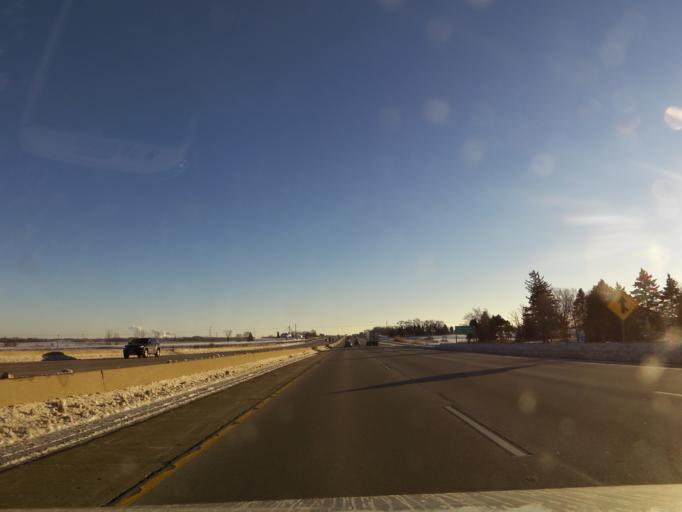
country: US
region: Wisconsin
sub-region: Kenosha County
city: Somers
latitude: 42.6395
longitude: -87.9527
